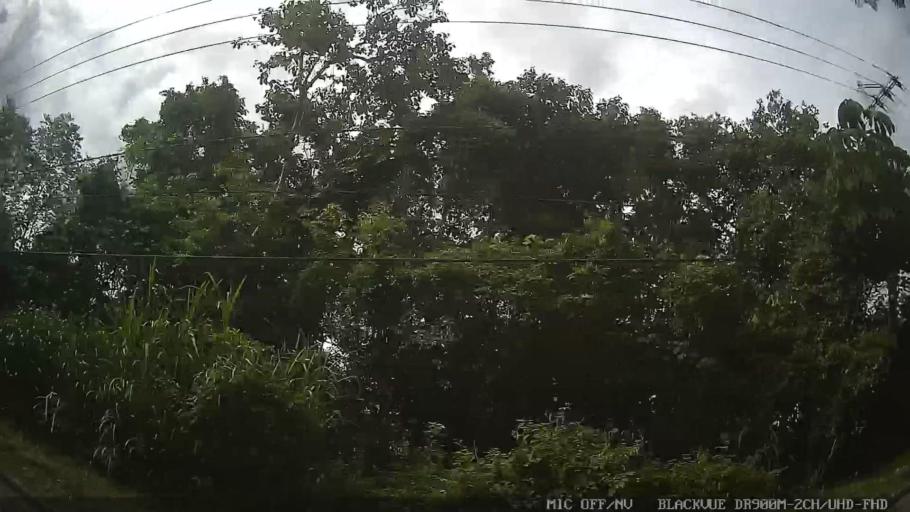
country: BR
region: Sao Paulo
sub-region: Mogi das Cruzes
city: Mogi das Cruzes
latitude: -23.5584
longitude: -46.1203
